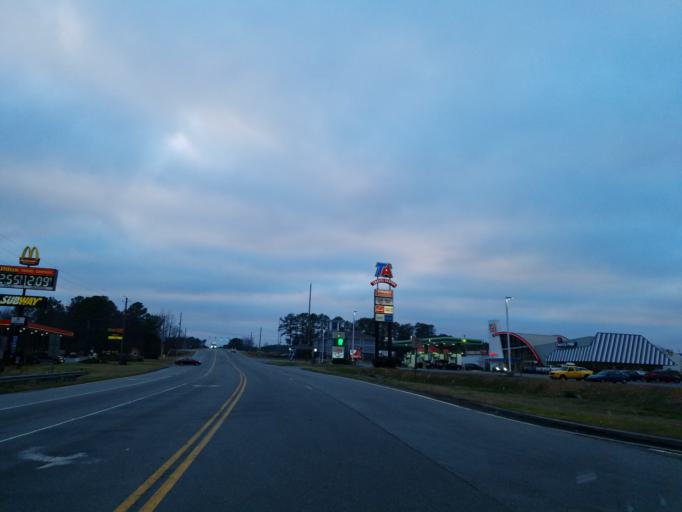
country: US
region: Georgia
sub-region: Bartow County
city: Cartersville
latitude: 34.2732
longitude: -84.8063
